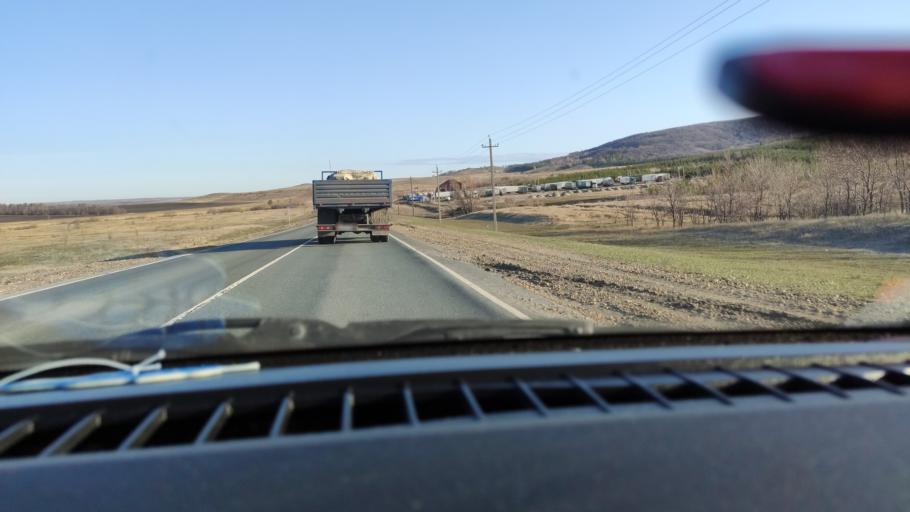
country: RU
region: Saratov
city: Alekseyevka
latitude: 52.3051
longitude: 47.9260
